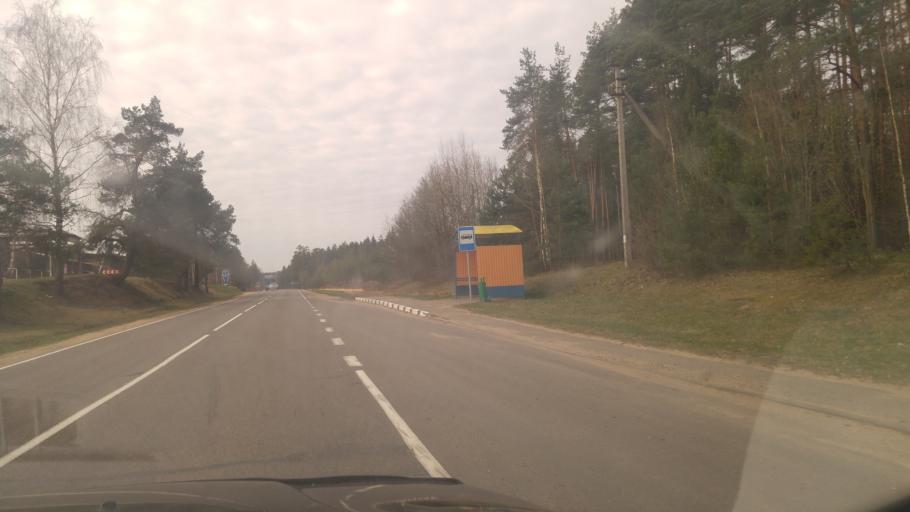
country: BY
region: Minsk
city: Chervyen'
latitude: 53.6999
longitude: 28.4059
